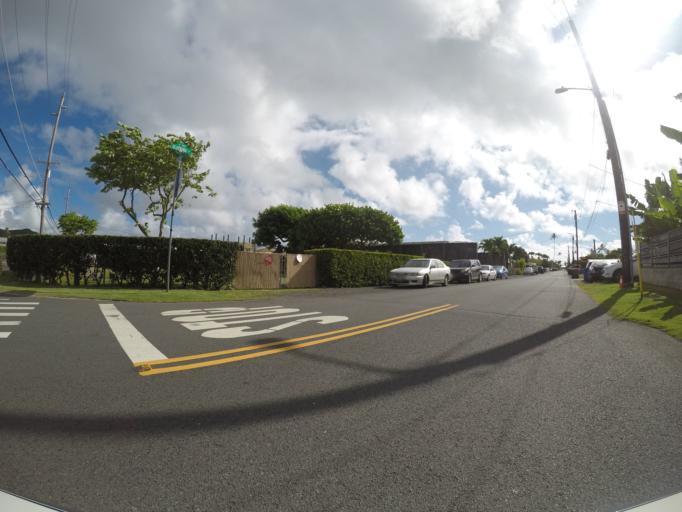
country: US
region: Hawaii
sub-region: Honolulu County
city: Kailua
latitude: 21.3999
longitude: -157.7477
